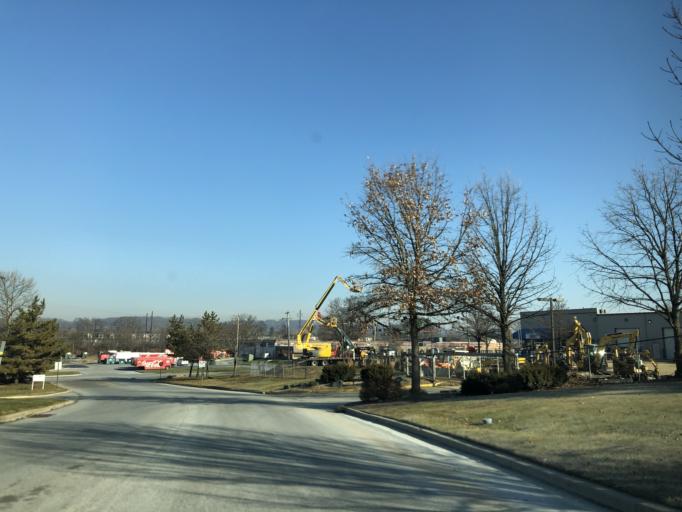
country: US
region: Pennsylvania
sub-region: Chester County
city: Downingtown
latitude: 40.0003
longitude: -75.6964
